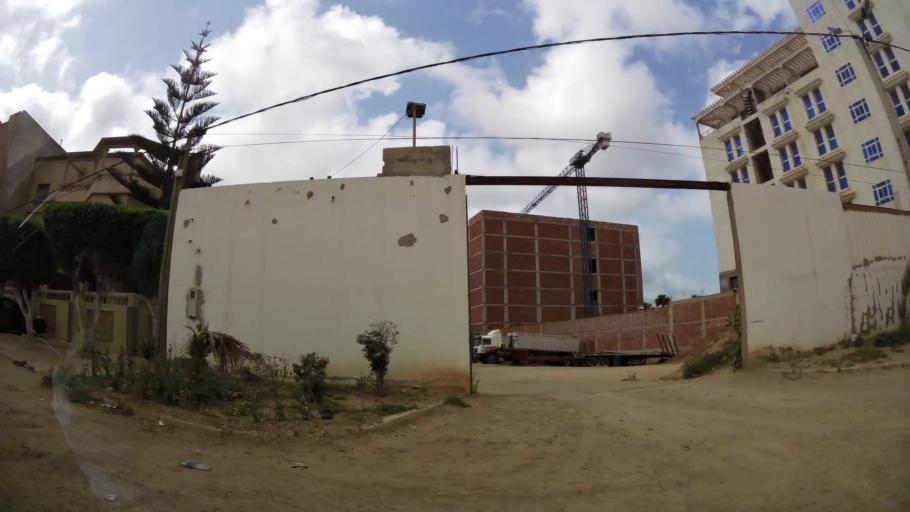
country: MA
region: Oriental
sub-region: Nador
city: Nador
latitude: 35.1585
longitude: -2.9310
